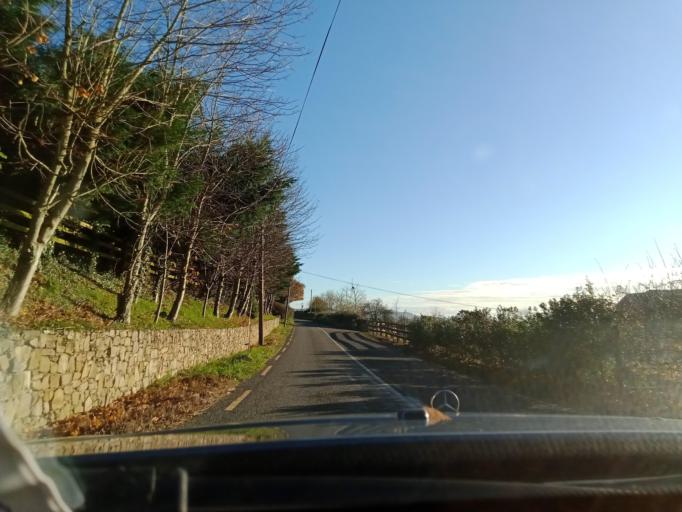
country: IE
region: Leinster
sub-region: Kilkenny
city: Piltown
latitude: 52.3955
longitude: -7.3673
